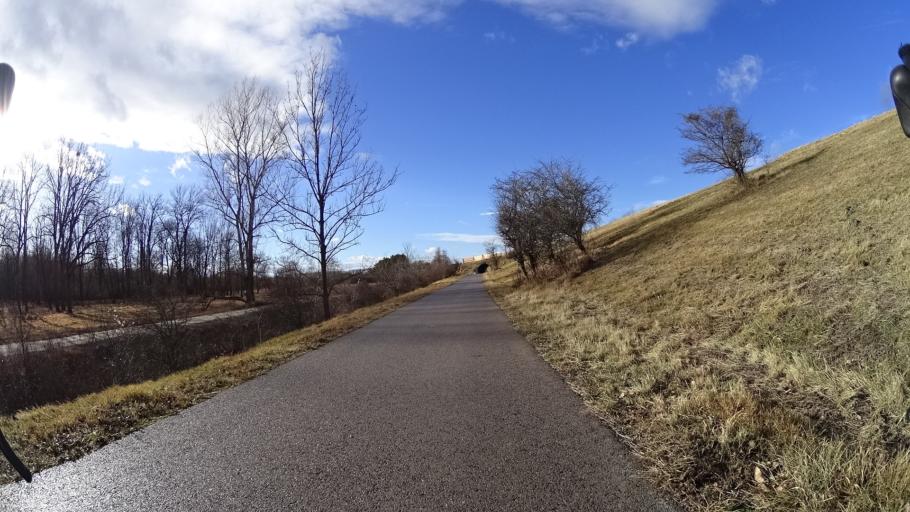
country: AT
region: Lower Austria
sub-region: Politischer Bezirk Tulln
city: Grafenworth
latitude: 48.3785
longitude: 15.8267
